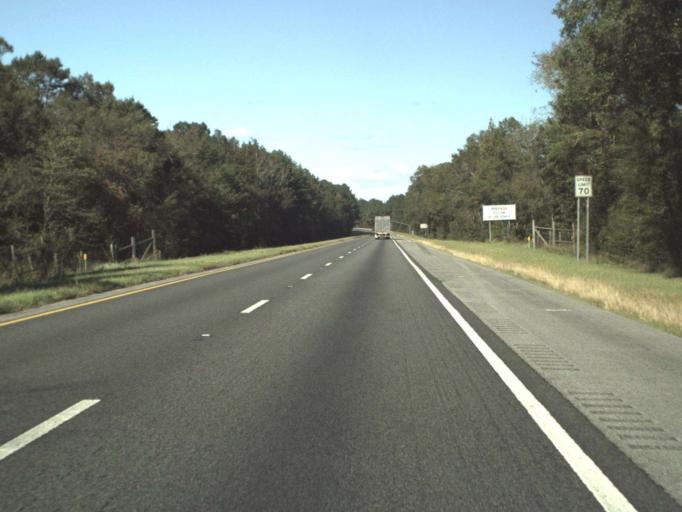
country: US
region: Florida
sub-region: Jackson County
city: Sneads
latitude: 30.6386
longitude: -84.9561
